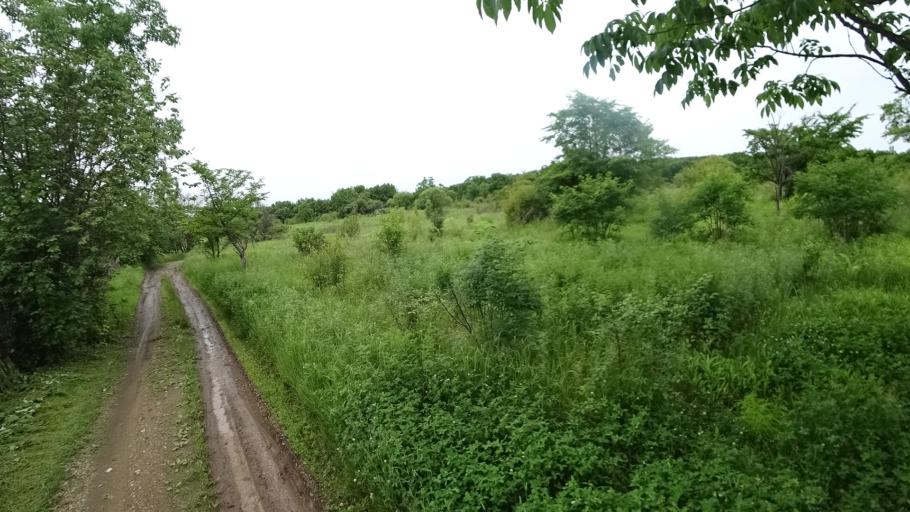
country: RU
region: Primorskiy
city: Novosysoyevka
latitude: 44.2104
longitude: 133.3272
